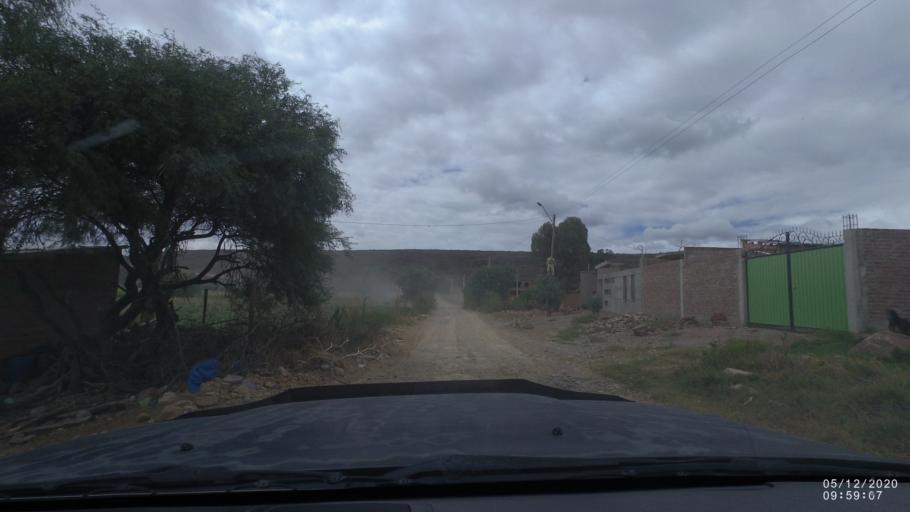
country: BO
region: Cochabamba
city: Sipe Sipe
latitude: -17.4334
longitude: -66.2917
